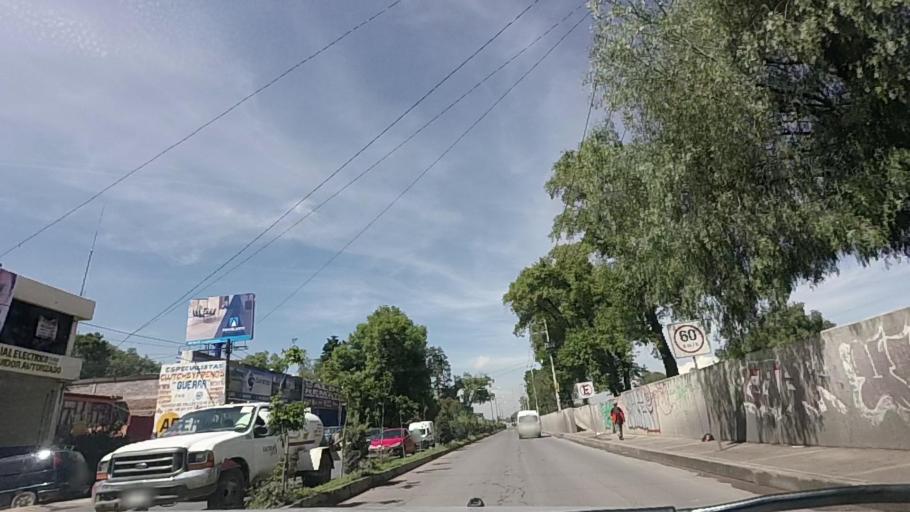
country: MX
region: Mexico
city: Teoloyucan
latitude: 19.7414
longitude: -99.1796
